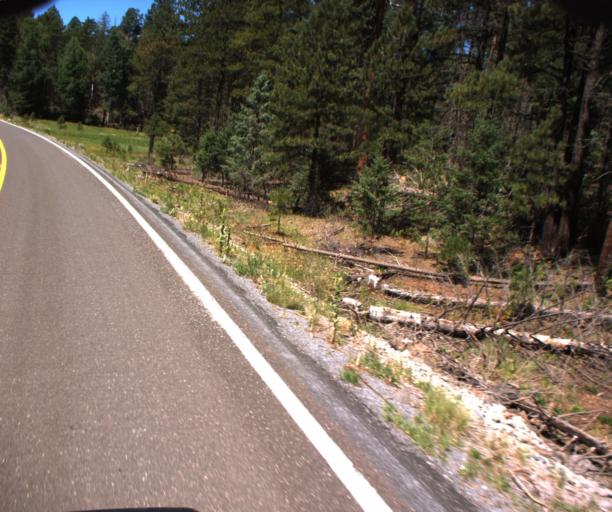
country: US
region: Arizona
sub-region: Apache County
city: Eagar
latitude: 33.6423
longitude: -109.3228
